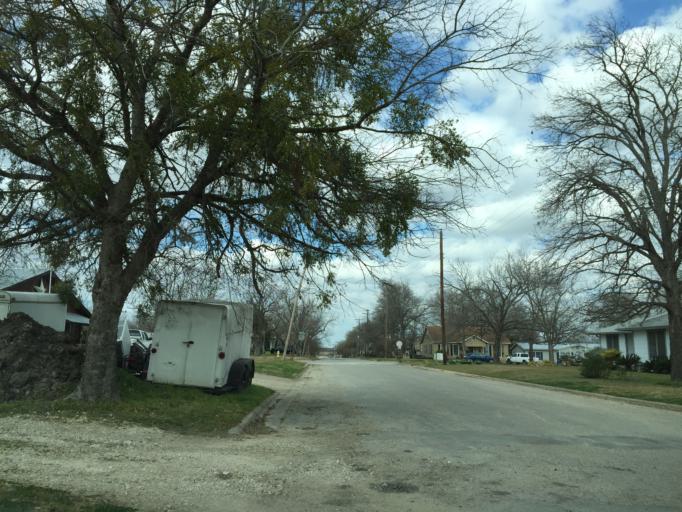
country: US
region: Texas
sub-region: Williamson County
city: Granger
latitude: 30.7180
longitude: -97.4406
